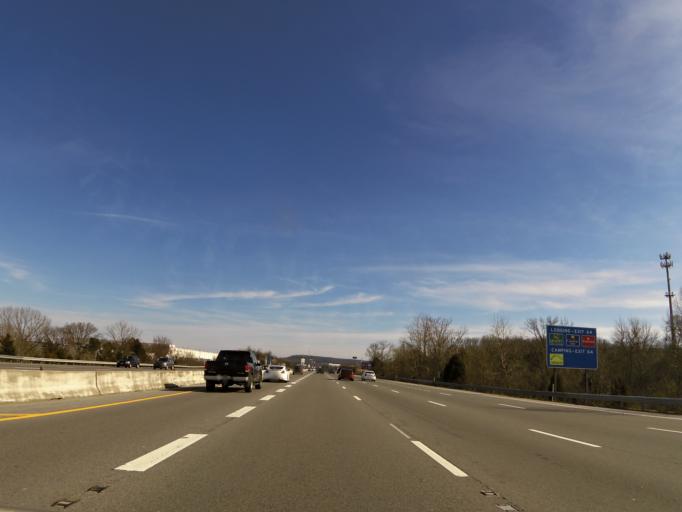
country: US
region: Tennessee
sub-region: Rutherford County
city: La Vergne
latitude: 36.0099
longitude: -86.6156
